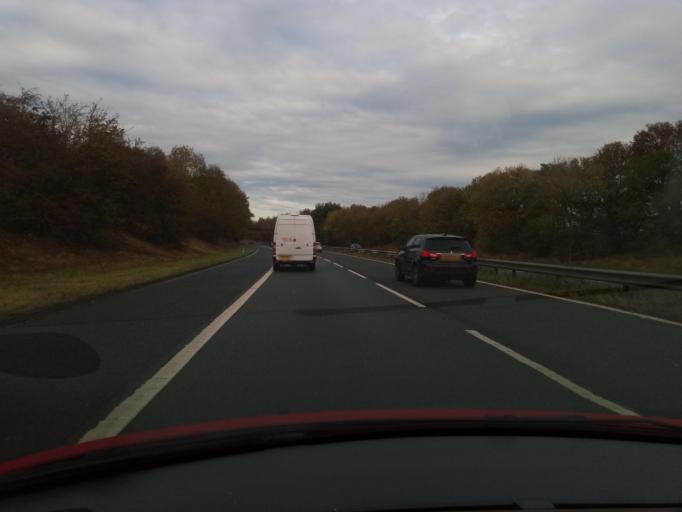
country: GB
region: England
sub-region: Darlington
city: High Coniscliffe
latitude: 54.5077
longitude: -1.6205
